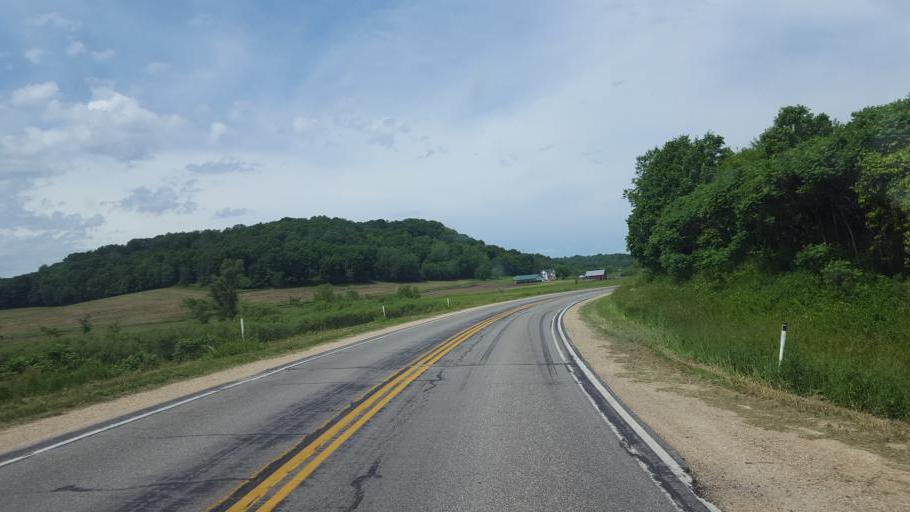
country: US
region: Wisconsin
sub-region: Vernon County
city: Hillsboro
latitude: 43.6439
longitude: -90.4128
